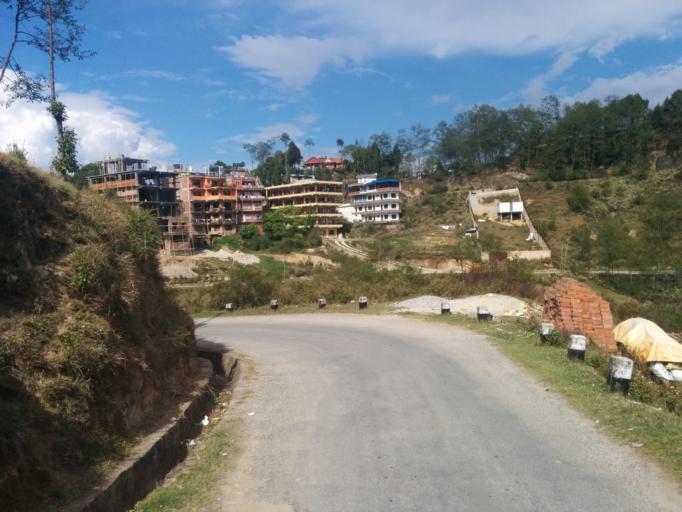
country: NP
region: Central Region
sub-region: Bagmati Zone
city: Nagarkot
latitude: 27.7173
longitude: 85.5179
